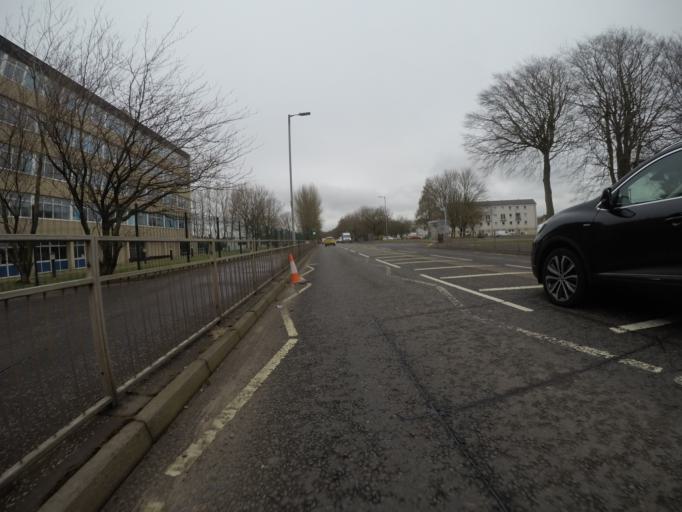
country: GB
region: Scotland
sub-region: North Ayrshire
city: Irvine
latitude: 55.6281
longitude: -4.6744
